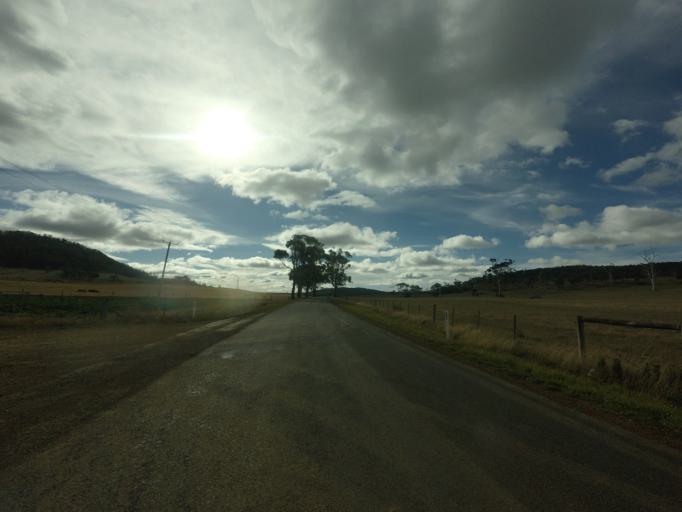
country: AU
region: Tasmania
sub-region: Brighton
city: Bridgewater
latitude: -42.3911
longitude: 147.3651
